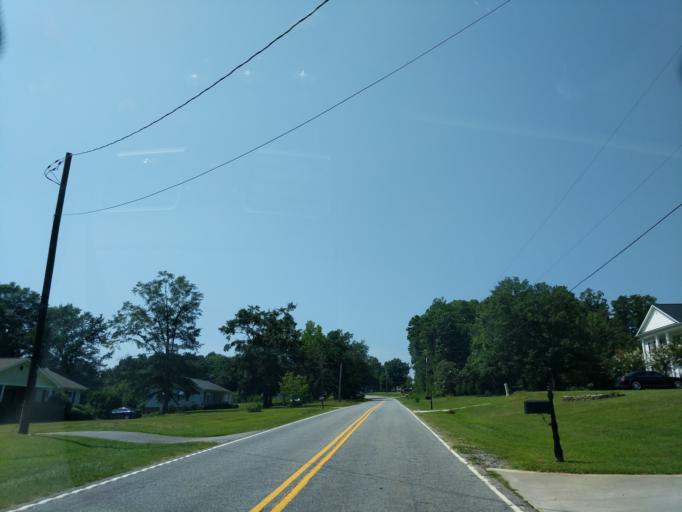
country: US
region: South Carolina
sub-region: Greenville County
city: Greer
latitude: 34.9677
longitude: -82.1948
